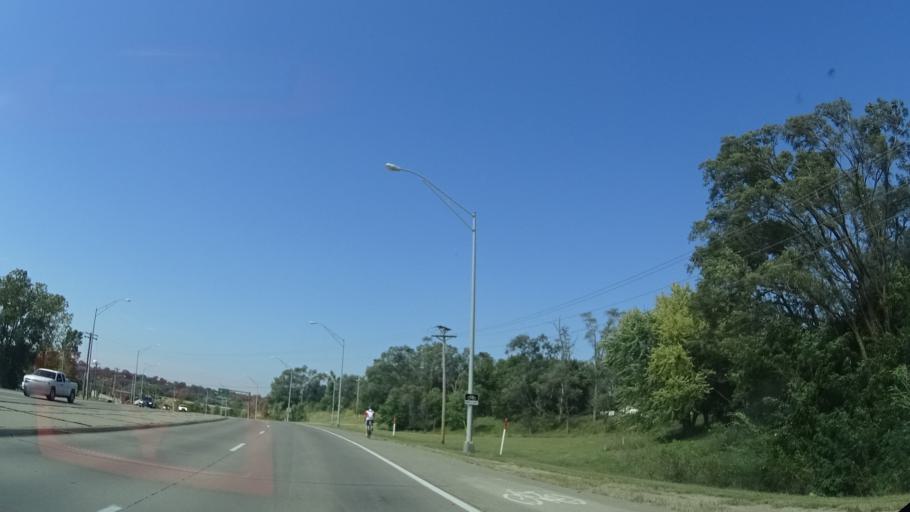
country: US
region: Nebraska
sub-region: Sarpy County
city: Offutt Air Force Base
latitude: 41.1174
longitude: -95.9306
